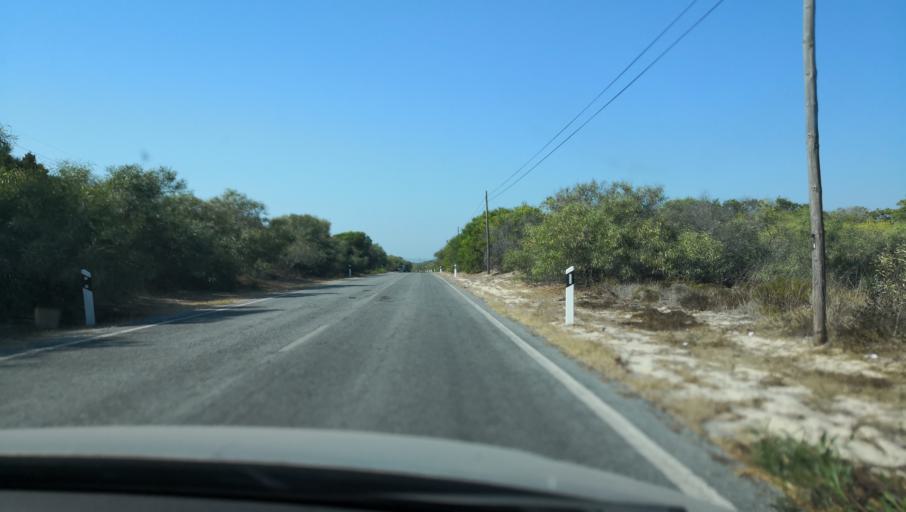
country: PT
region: Setubal
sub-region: Setubal
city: Setubal
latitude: 38.4049
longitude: -8.8089
